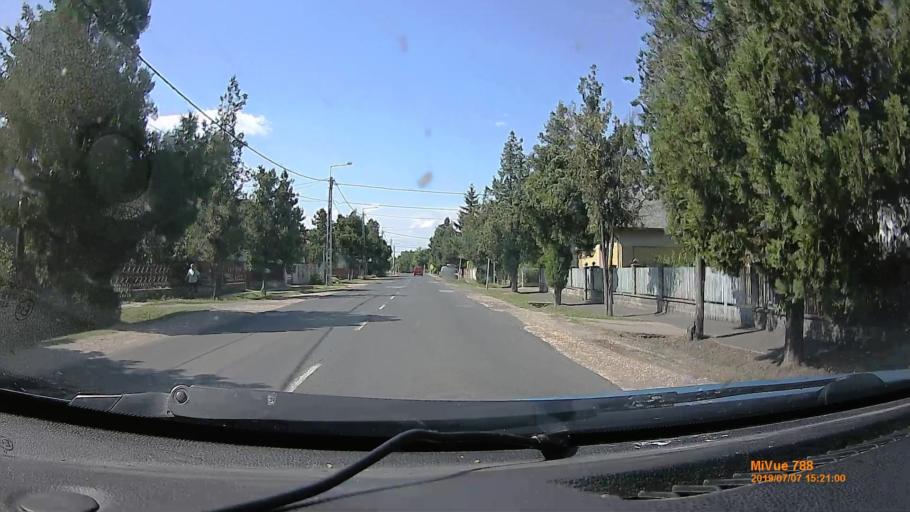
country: HU
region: Jasz-Nagykun-Szolnok
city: Jaszalsoszentgyorgy
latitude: 47.3736
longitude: 20.0901
